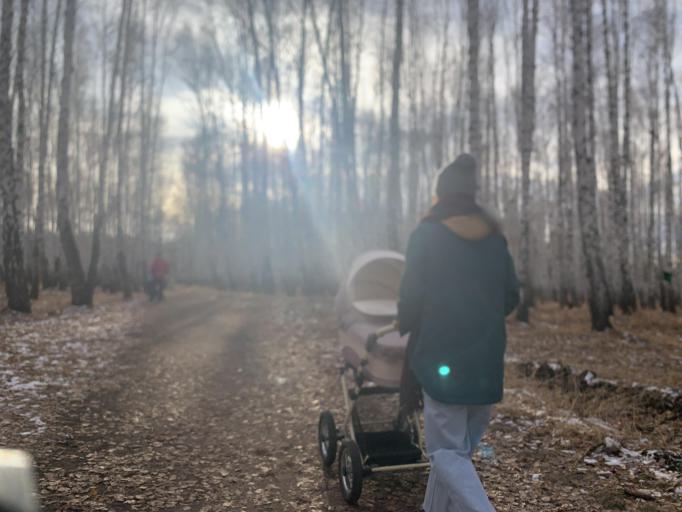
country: RU
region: Chelyabinsk
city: Roshchino
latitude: 55.2046
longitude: 61.3046
